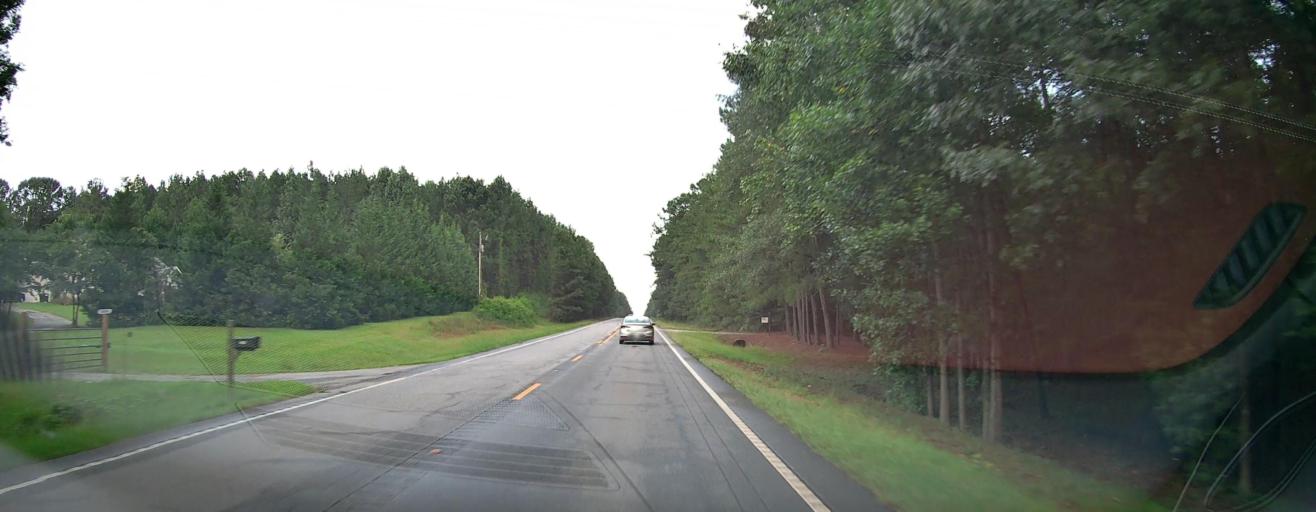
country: US
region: Georgia
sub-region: Coweta County
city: Senoia
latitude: 33.2731
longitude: -84.5536
